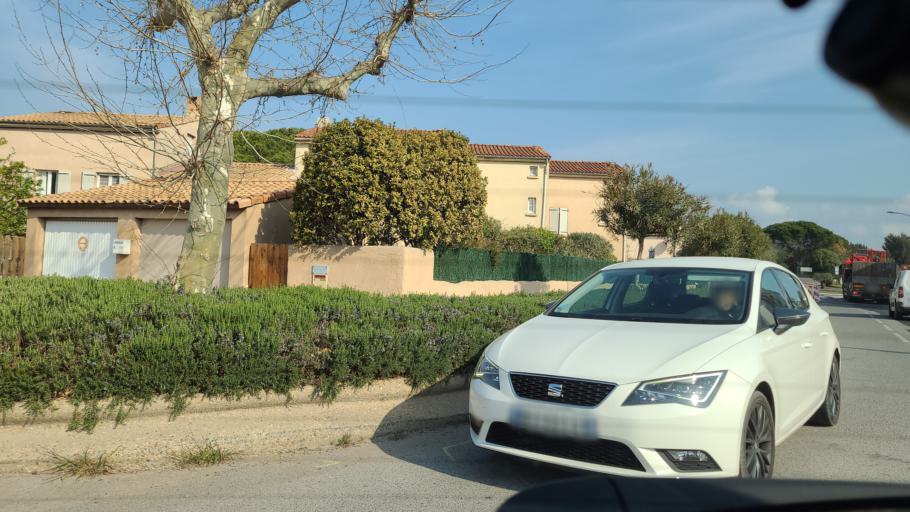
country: FR
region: Provence-Alpes-Cote d'Azur
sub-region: Departement du Var
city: Puget-sur-Argens
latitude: 43.4549
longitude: 6.6934
